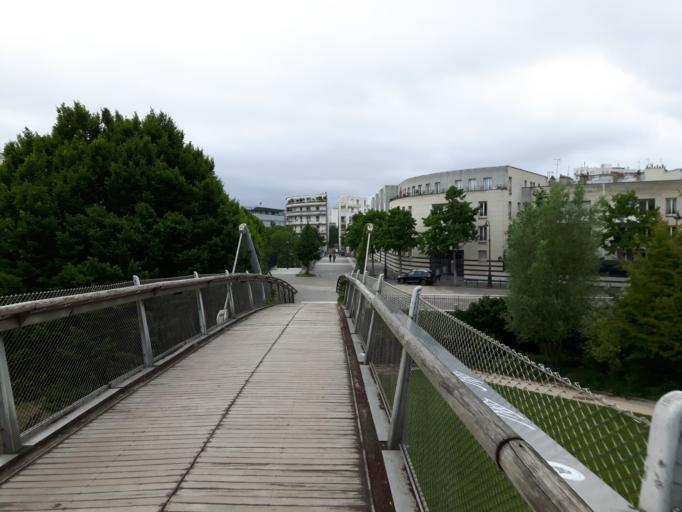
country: FR
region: Ile-de-France
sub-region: Departement du Val-de-Marne
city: Ivry-sur-Seine
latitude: 48.8422
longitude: 2.3879
